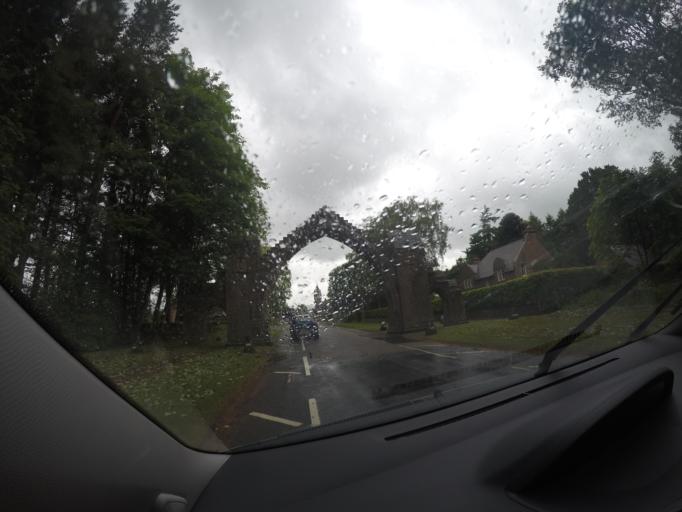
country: GB
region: Scotland
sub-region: Angus
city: Brechin
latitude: 56.8051
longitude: -2.6535
